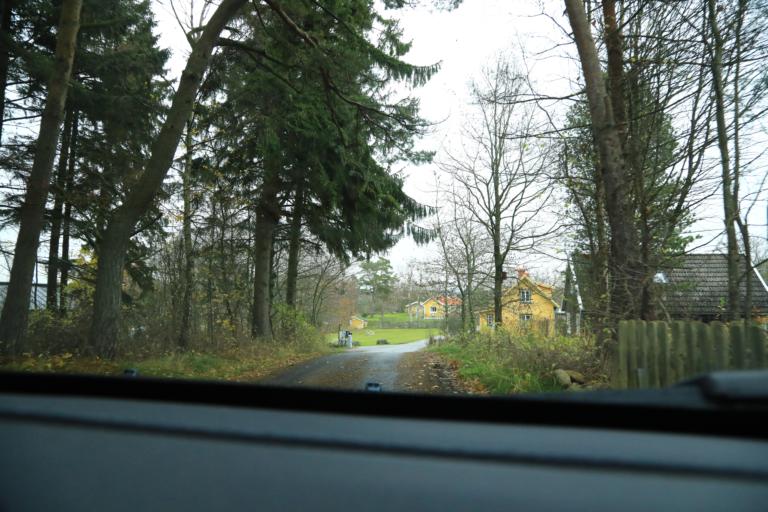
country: SE
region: Halland
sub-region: Varbergs Kommun
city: Varberg
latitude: 57.1697
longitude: 12.2142
